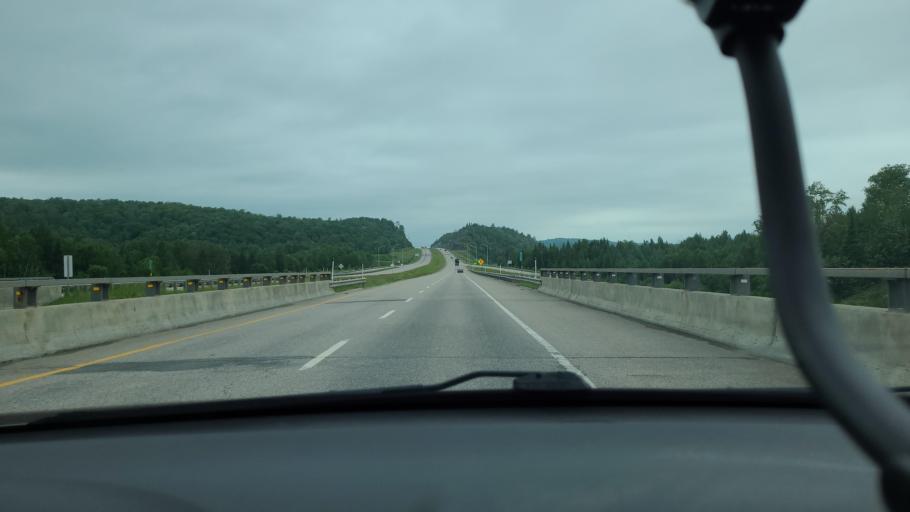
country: CA
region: Quebec
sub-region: Laurentides
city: Labelle
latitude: 46.2567
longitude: -74.7239
